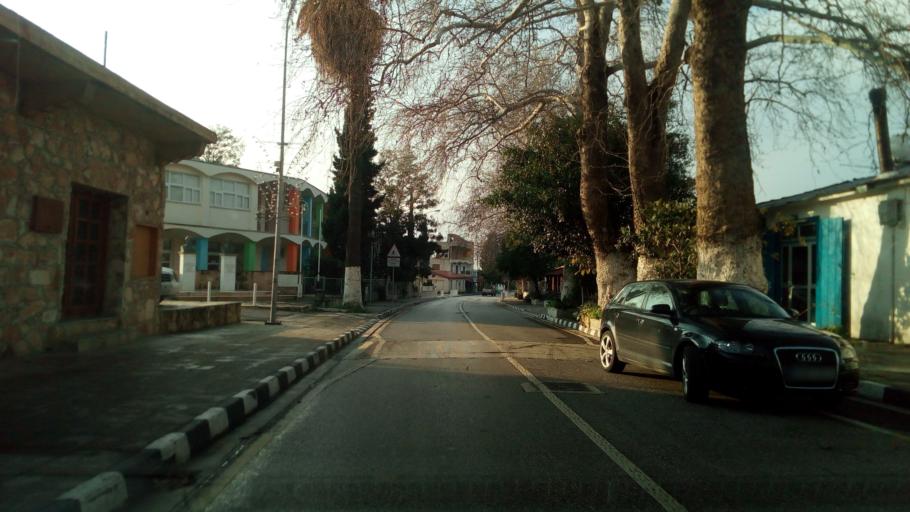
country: CY
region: Lefkosia
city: Kato Pyrgos
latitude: 35.1823
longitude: 32.6840
